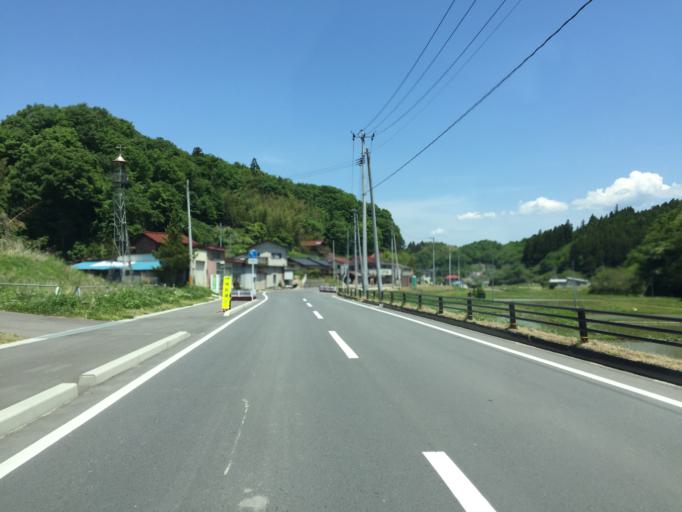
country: JP
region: Fukushima
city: Funehikimachi-funehiki
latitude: 37.4863
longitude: 140.5449
